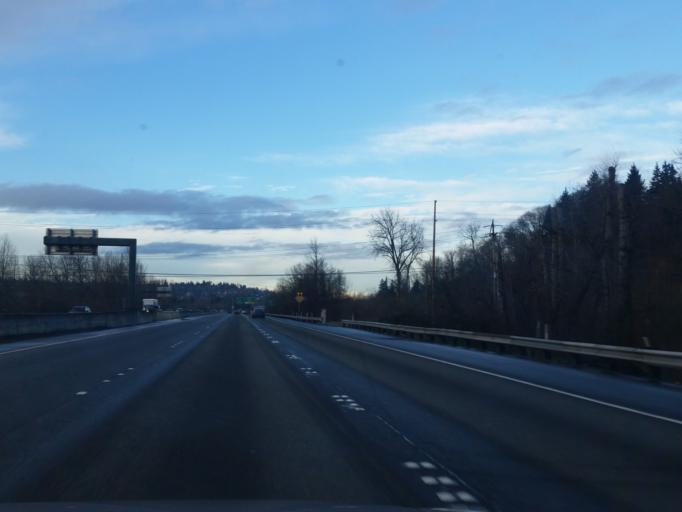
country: US
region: Washington
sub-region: King County
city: Renton
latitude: 47.4580
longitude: -122.2168
